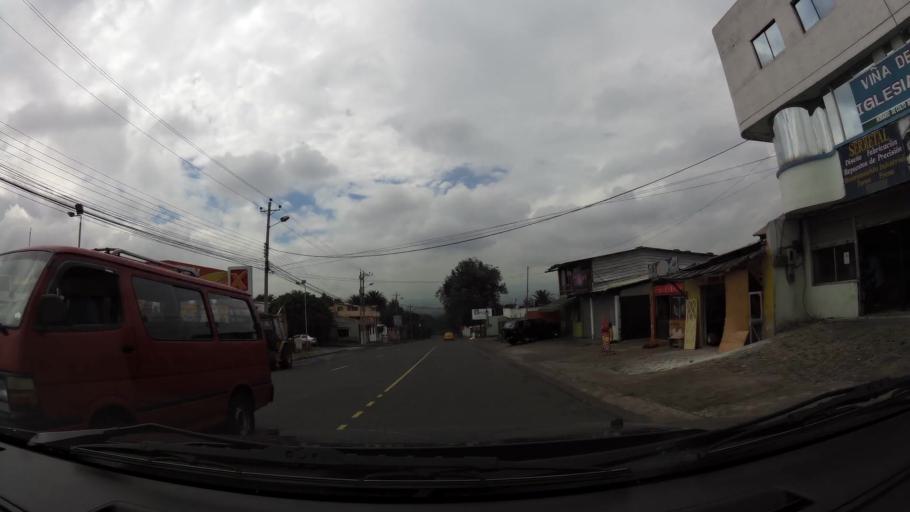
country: EC
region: Pichincha
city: Sangolqui
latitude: -0.3041
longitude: -78.4784
